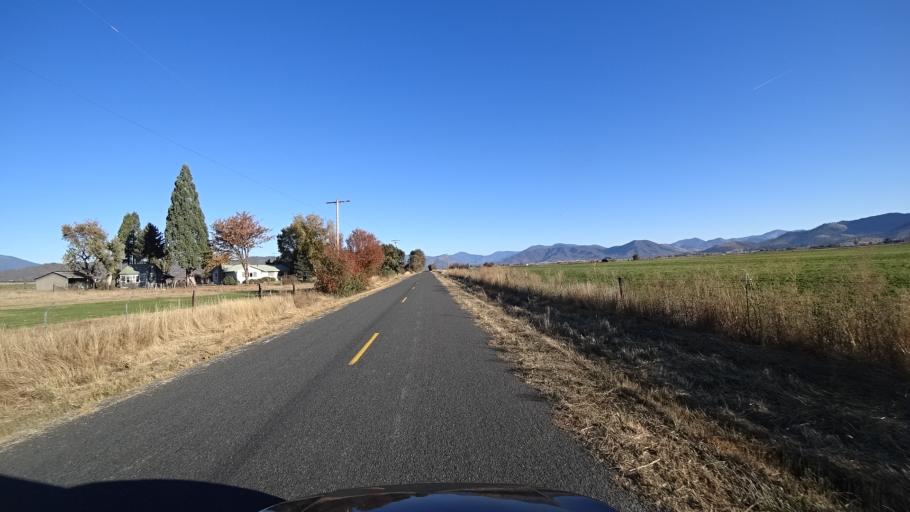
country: US
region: California
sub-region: Siskiyou County
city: Yreka
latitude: 41.5278
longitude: -122.8580
